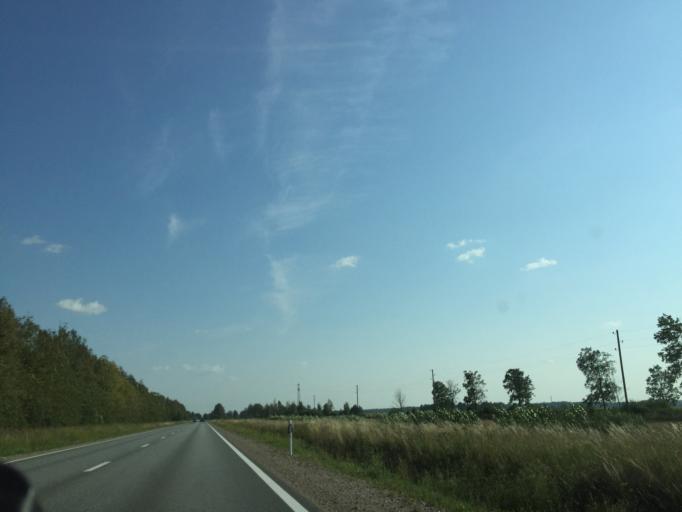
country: LV
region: Jelgava
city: Jelgava
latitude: 56.4427
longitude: 23.6887
